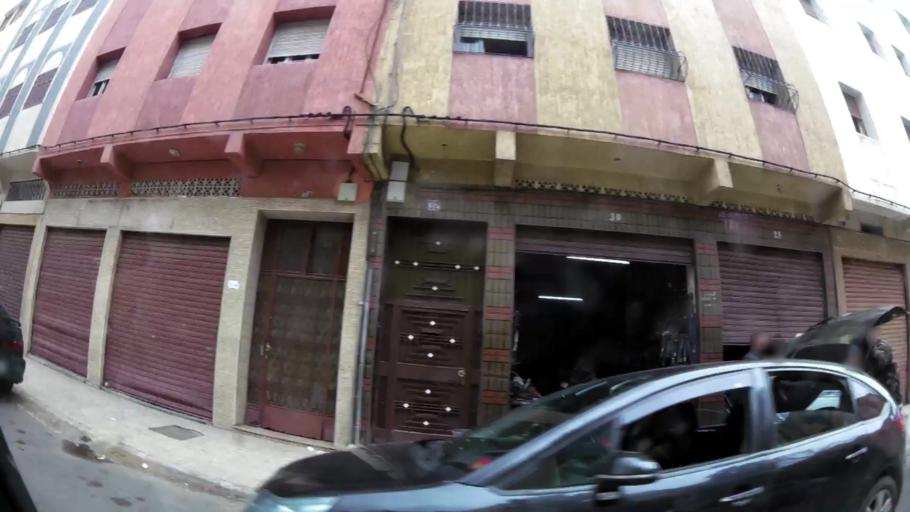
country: MA
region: Grand Casablanca
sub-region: Mediouna
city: Tit Mellil
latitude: 33.6096
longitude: -7.4936
